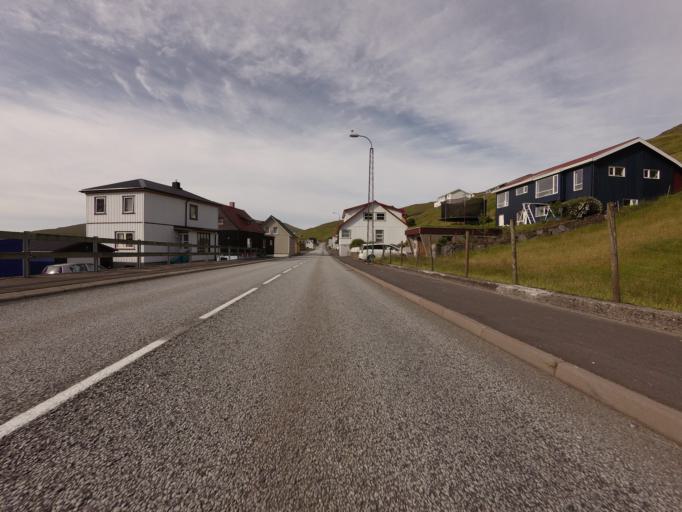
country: FO
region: Vagar
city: Midvagur
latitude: 62.0558
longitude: -7.1527
